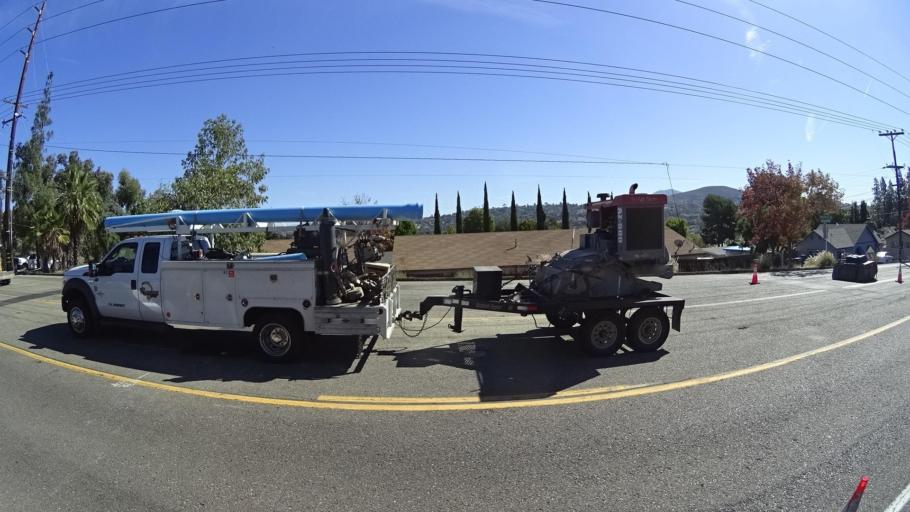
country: US
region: California
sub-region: San Diego County
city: Spring Valley
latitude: 32.7401
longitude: -117.0145
